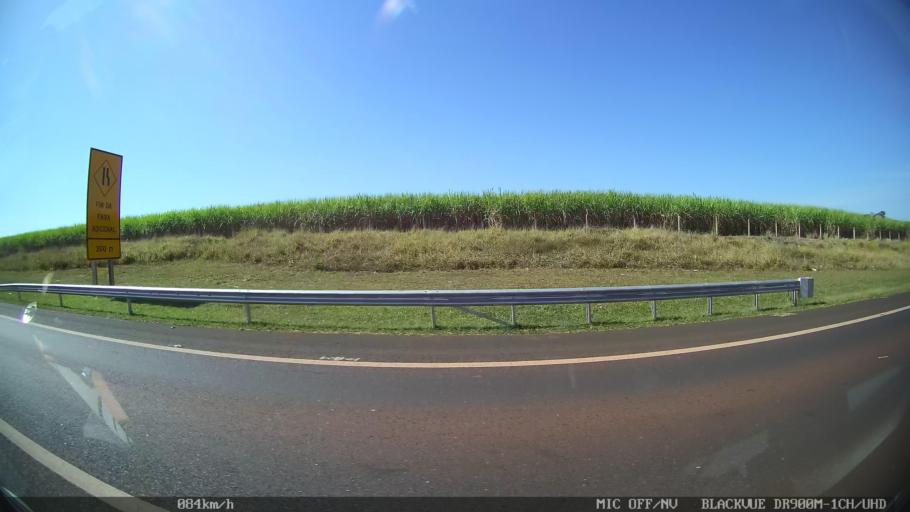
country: BR
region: Sao Paulo
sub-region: Batatais
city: Batatais
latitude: -20.8373
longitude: -47.6014
